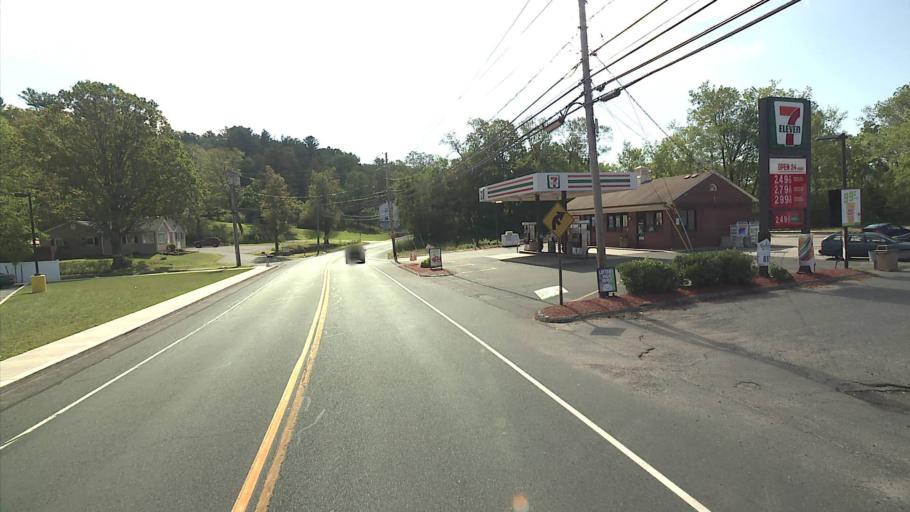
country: US
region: Connecticut
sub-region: Tolland County
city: Stafford Springs
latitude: 41.9598
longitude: -72.3134
